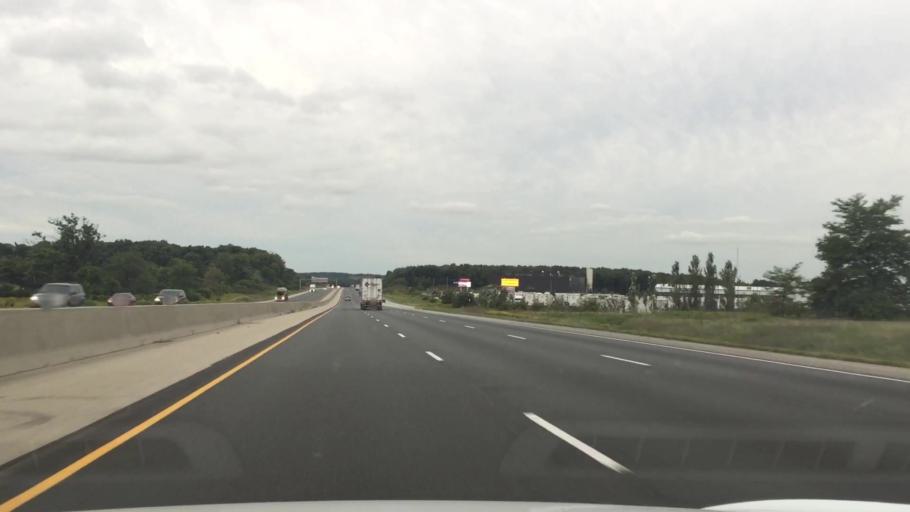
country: CA
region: Ontario
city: Kitchener
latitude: 43.3279
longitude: -80.4519
